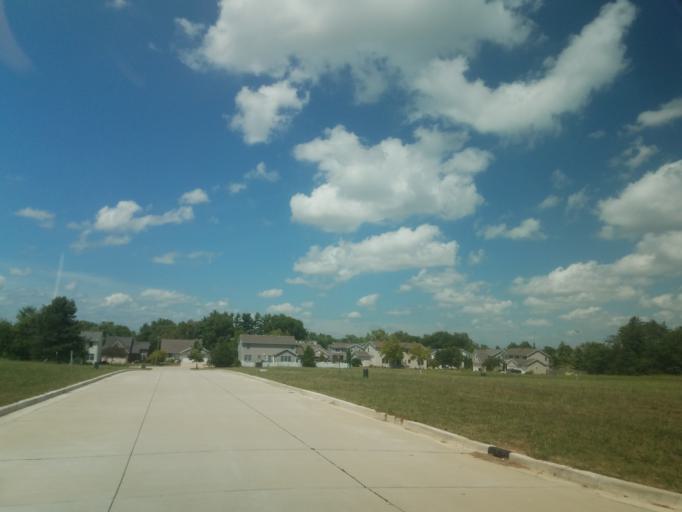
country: US
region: Illinois
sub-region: McLean County
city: Bloomington
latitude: 40.4479
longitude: -89.0312
